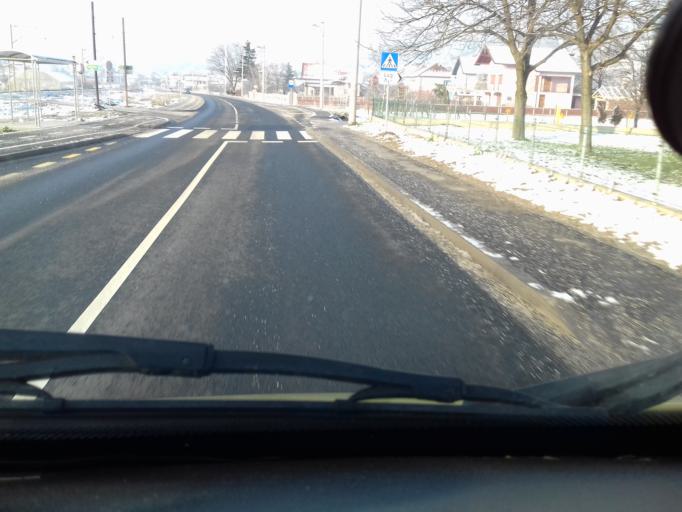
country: BA
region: Federation of Bosnia and Herzegovina
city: Mahala
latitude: 43.9829
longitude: 18.2391
